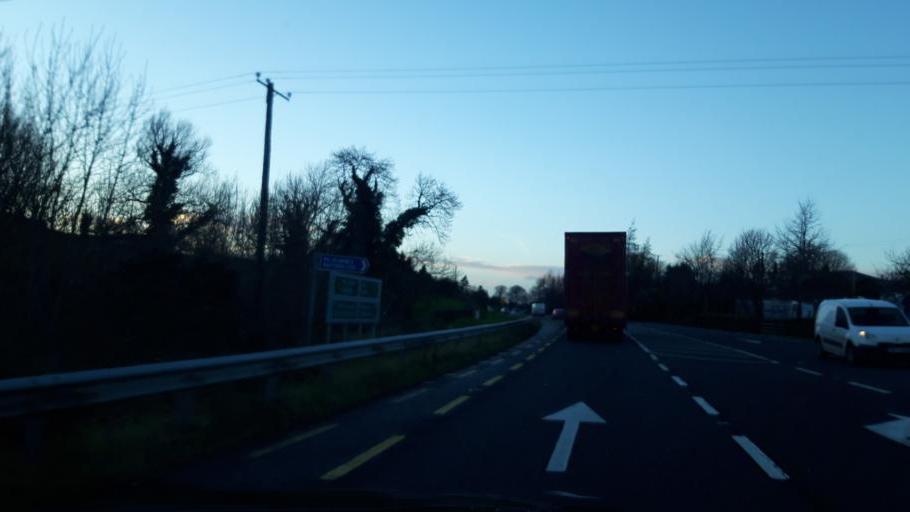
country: IE
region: Ulster
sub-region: County Monaghan
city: Monaghan
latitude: 54.2394
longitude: -6.9272
